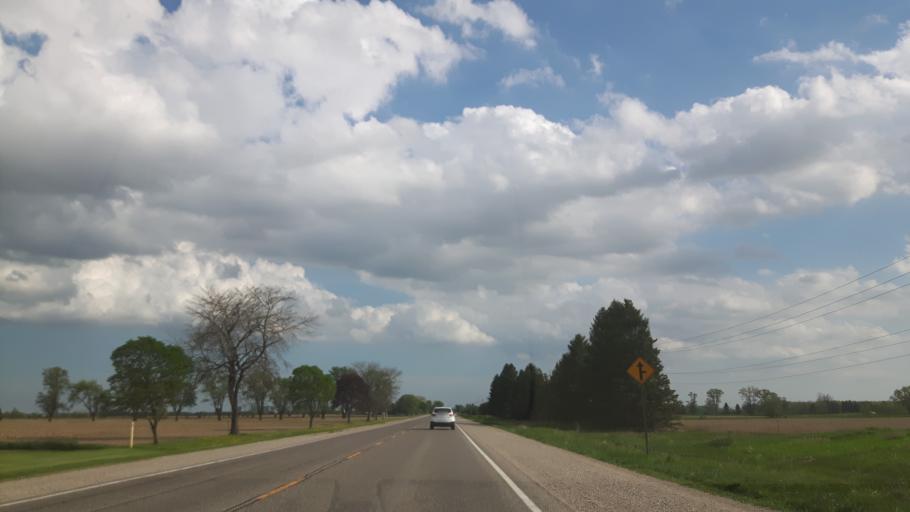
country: CA
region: Ontario
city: South Huron
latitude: 43.2674
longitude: -81.4647
